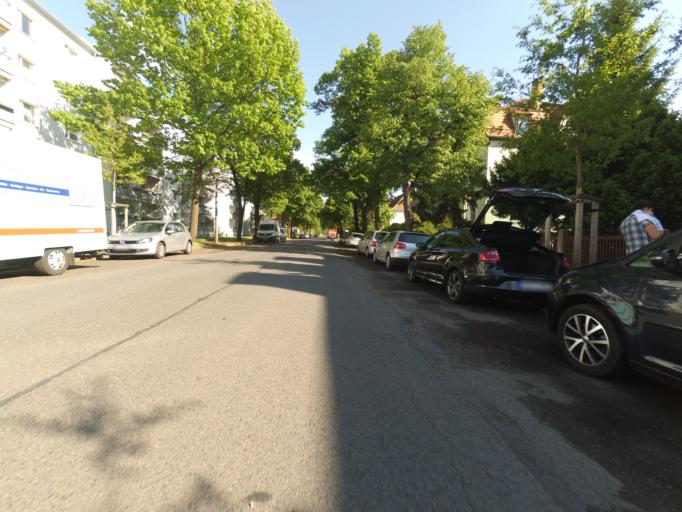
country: DE
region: Saxony
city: Heidenau
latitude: 51.0169
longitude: 13.8114
